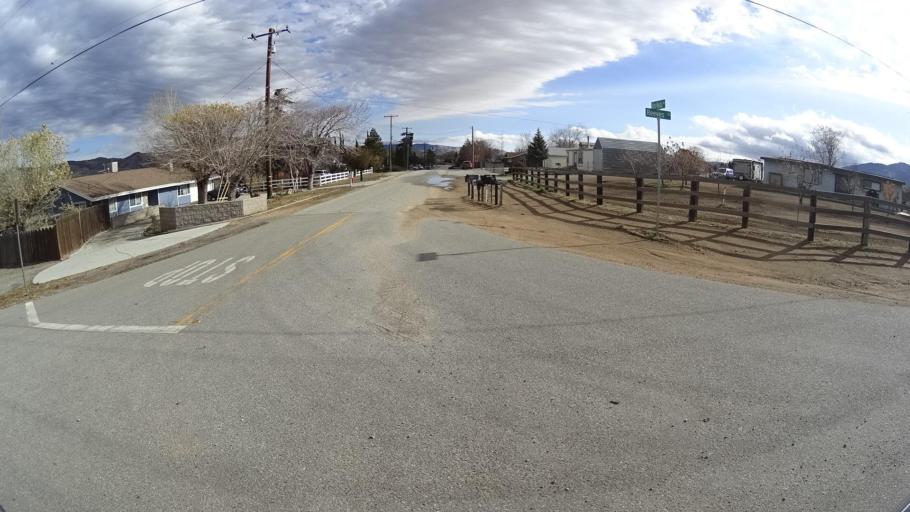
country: US
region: California
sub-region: Kern County
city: Golden Hills
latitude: 35.1289
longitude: -118.4768
